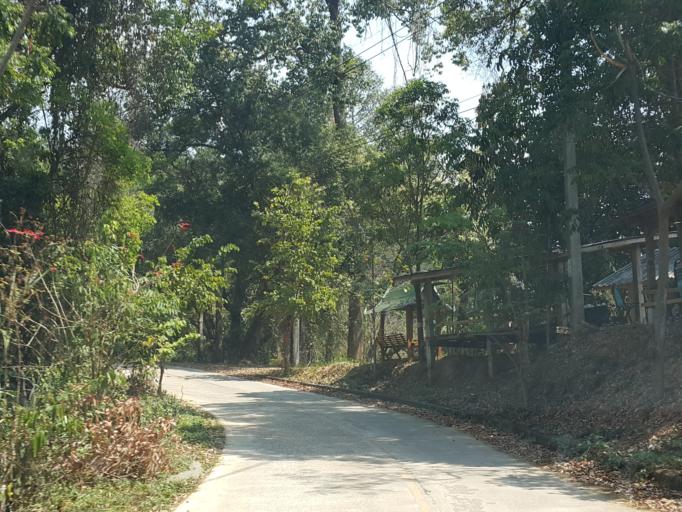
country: TH
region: Lampang
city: Mueang Pan
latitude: 18.8269
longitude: 99.3910
